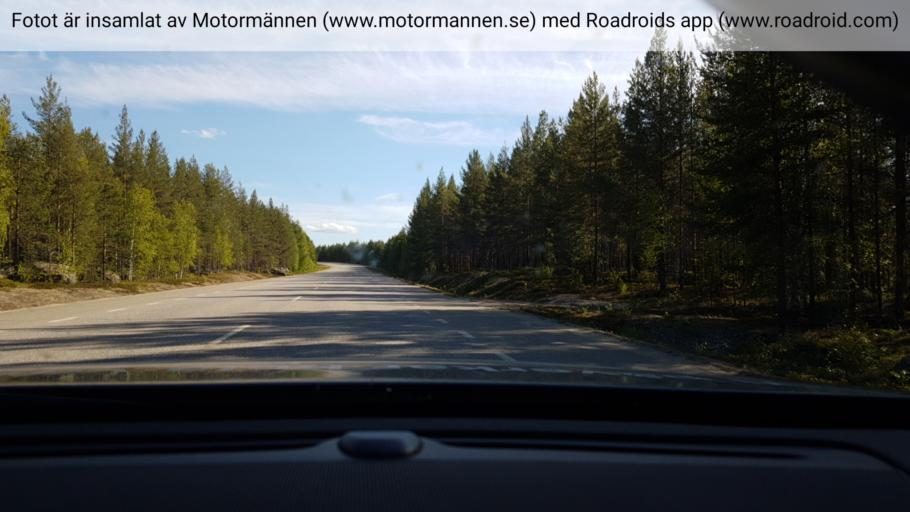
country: SE
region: Vaesterbotten
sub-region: Norsjo Kommun
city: Norsjoe
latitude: 64.5933
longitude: 19.2982
